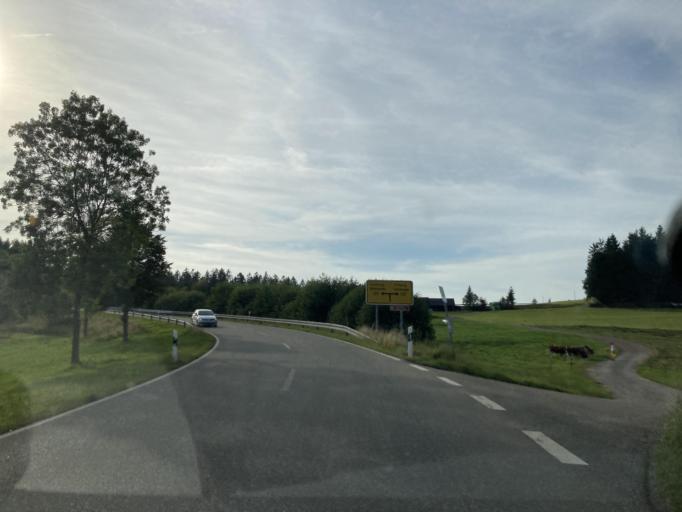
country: DE
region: Baden-Wuerttemberg
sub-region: Freiburg Region
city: Gutenbach
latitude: 47.9851
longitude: 8.1557
